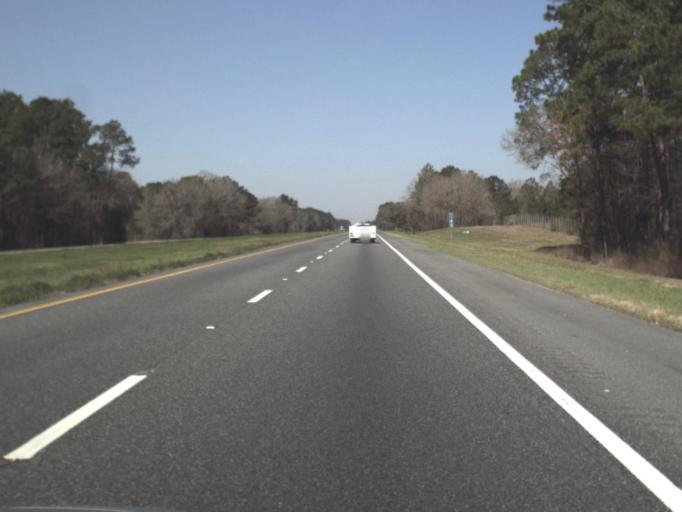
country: US
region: Florida
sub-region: Jackson County
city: Marianna
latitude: 30.7015
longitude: -85.1368
